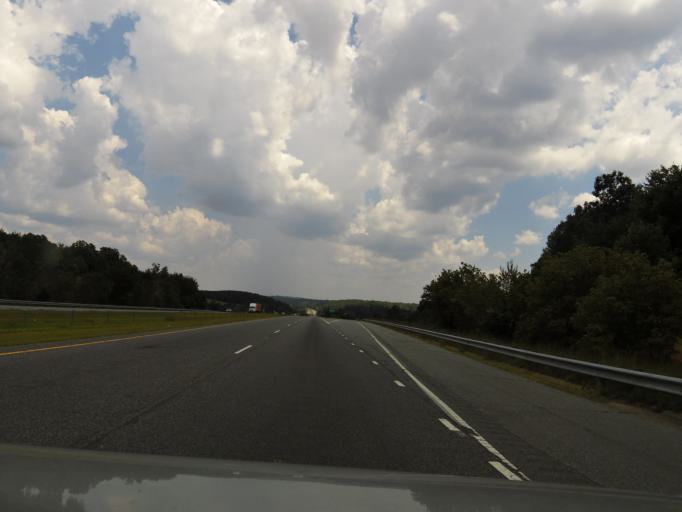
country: US
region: North Carolina
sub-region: Rutherford County
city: Rutherfordton
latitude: 35.2910
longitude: -82.0118
